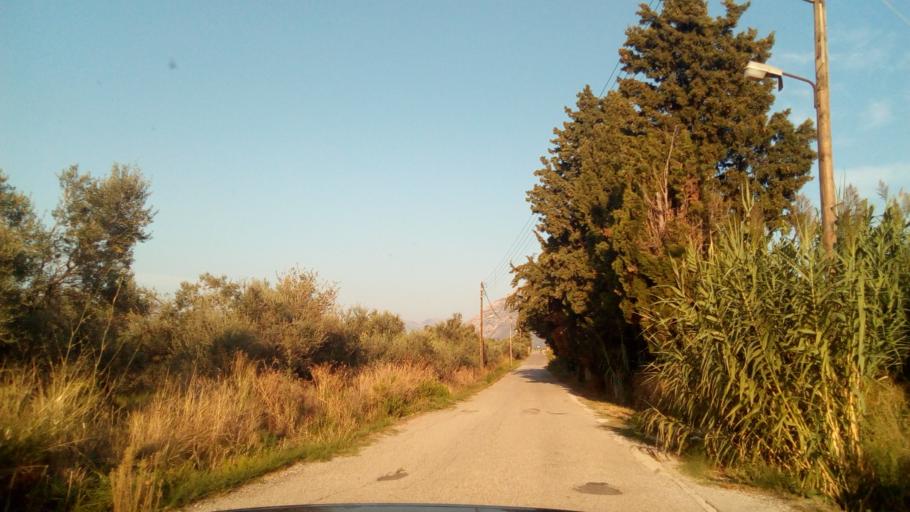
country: GR
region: West Greece
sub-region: Nomos Aitolias kai Akarnanias
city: Antirrio
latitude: 38.3367
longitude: 21.7471
